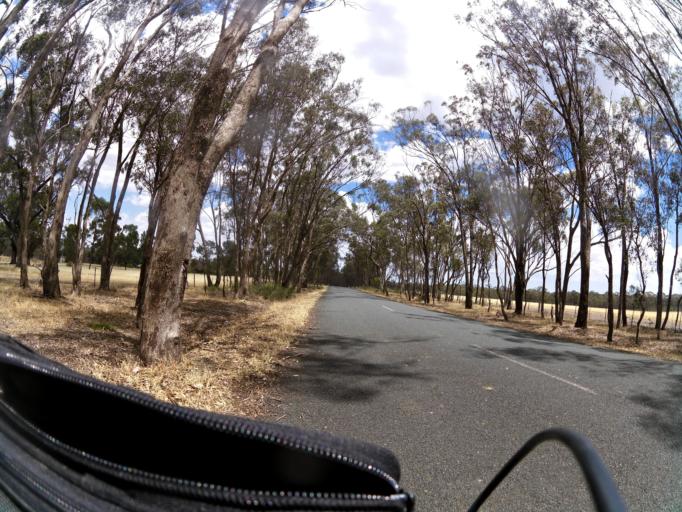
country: AU
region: Victoria
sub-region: Greater Shepparton
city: Shepparton
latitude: -36.6818
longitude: 145.1916
